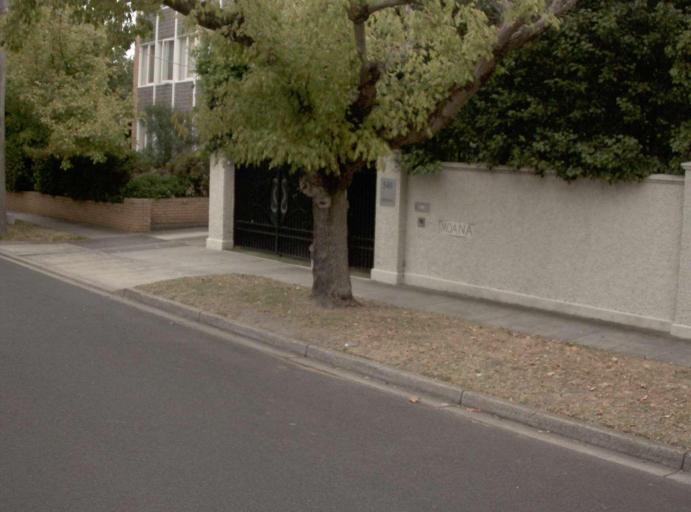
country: AU
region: Victoria
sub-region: Port Phillip
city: St Kilda East
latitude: -37.8564
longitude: 145.0112
